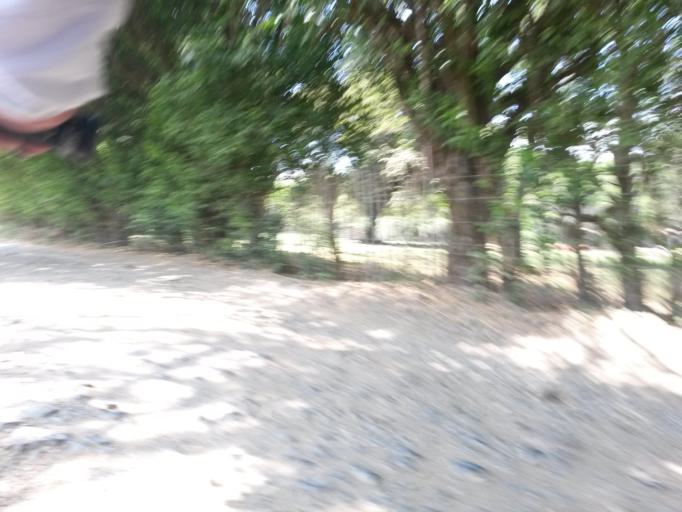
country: CO
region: Cauca
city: Santander de Quilichao
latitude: 3.0127
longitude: -76.4784
